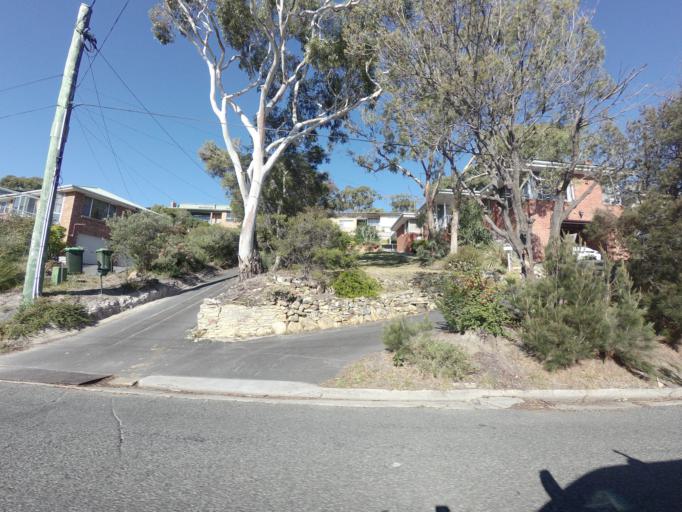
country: AU
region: Tasmania
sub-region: Clarence
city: Lindisfarne
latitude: -42.8427
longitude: 147.3400
